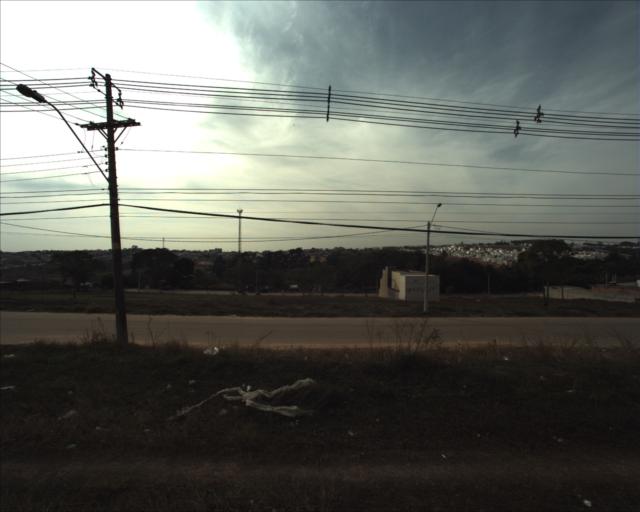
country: BR
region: Sao Paulo
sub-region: Sorocaba
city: Sorocaba
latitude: -23.4425
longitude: -47.5148
